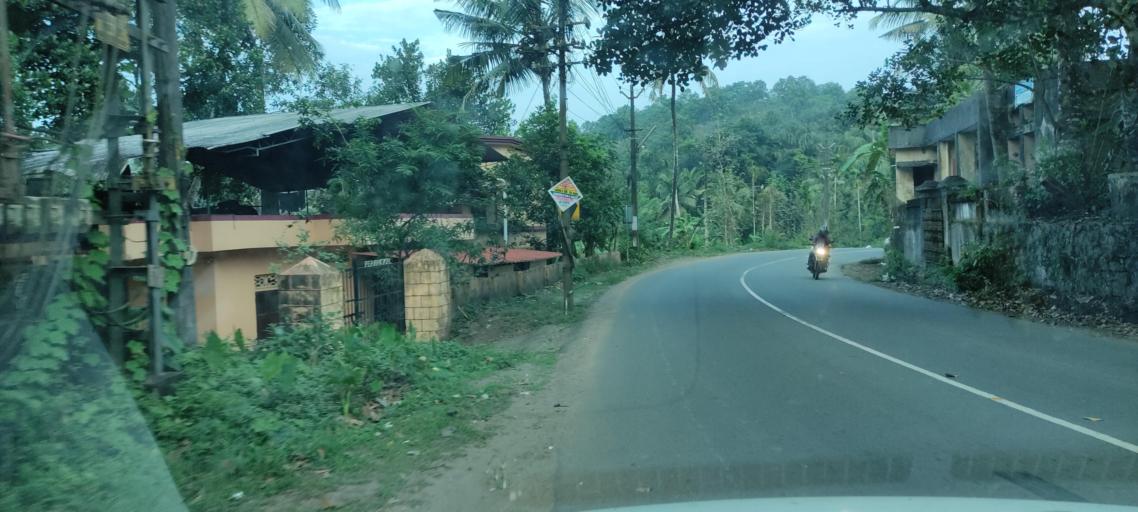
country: IN
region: Kerala
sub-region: Pattanamtitta
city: Adur
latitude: 9.1226
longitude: 76.7002
